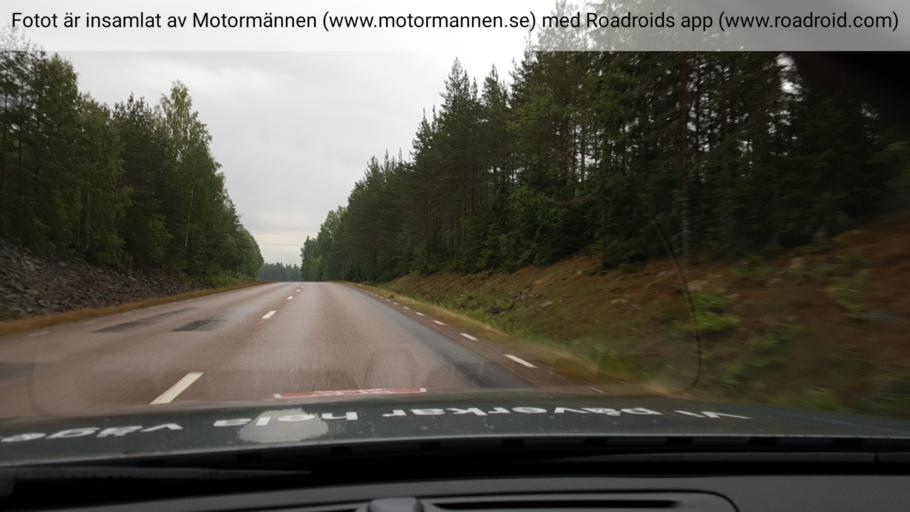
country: SE
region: Dalarna
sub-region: Avesta Kommun
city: Avesta
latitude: 59.9653
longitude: 16.1885
